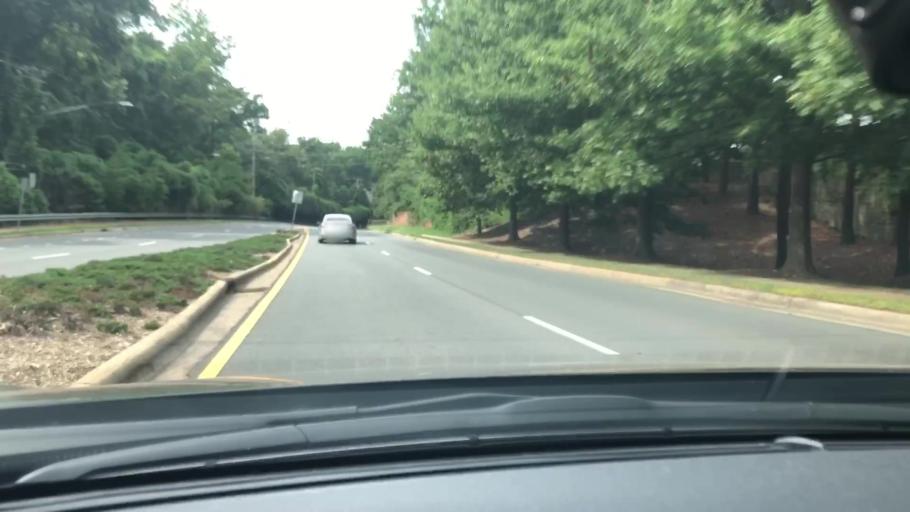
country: US
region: North Carolina
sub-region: Mecklenburg County
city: Charlotte
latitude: 35.1852
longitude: -80.8083
